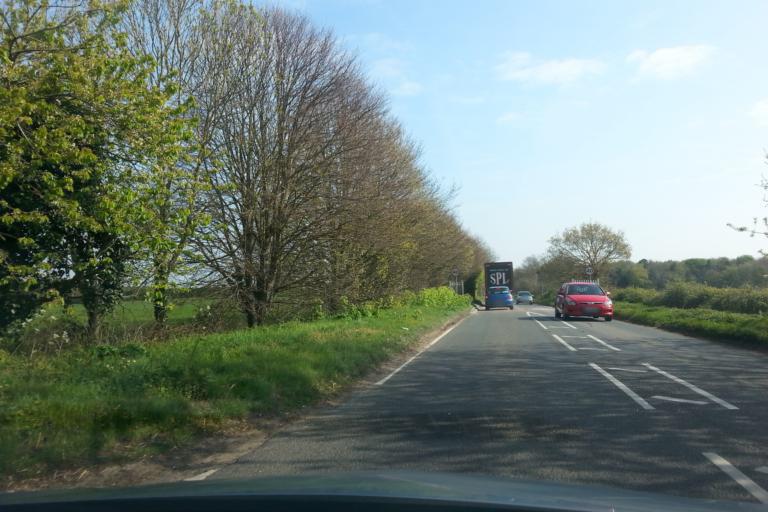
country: GB
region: England
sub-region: Suffolk
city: Wickham Market
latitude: 52.1188
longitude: 1.3870
